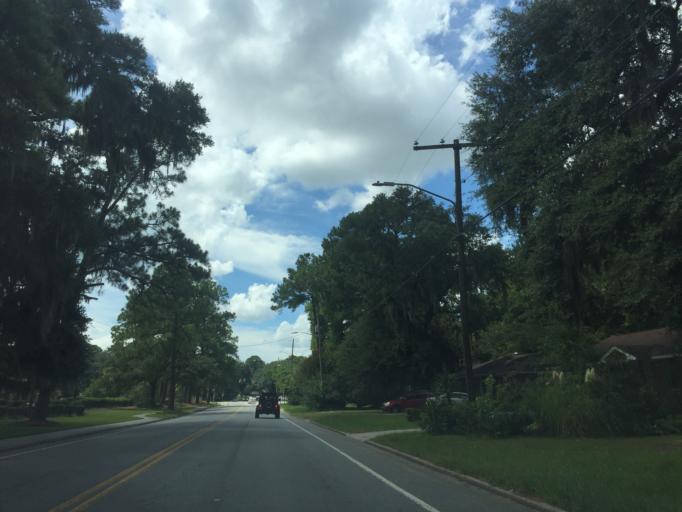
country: US
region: Georgia
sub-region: Chatham County
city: Savannah
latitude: 32.0293
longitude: -81.1054
